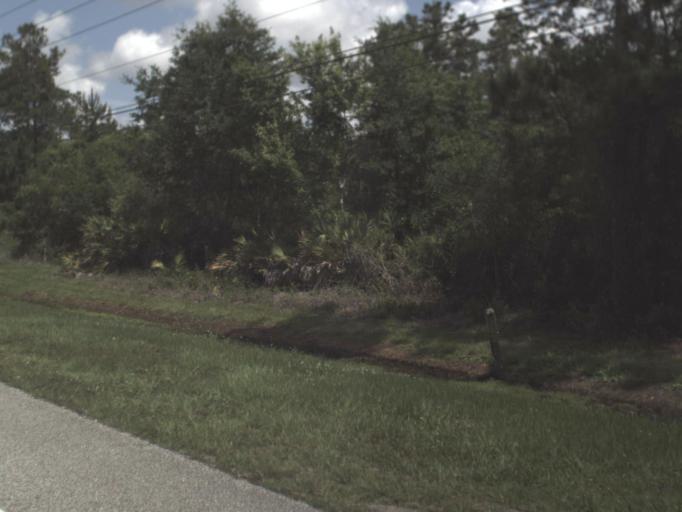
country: US
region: Florida
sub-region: Saint Johns County
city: Palm Valley
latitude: 30.1213
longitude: -81.4956
